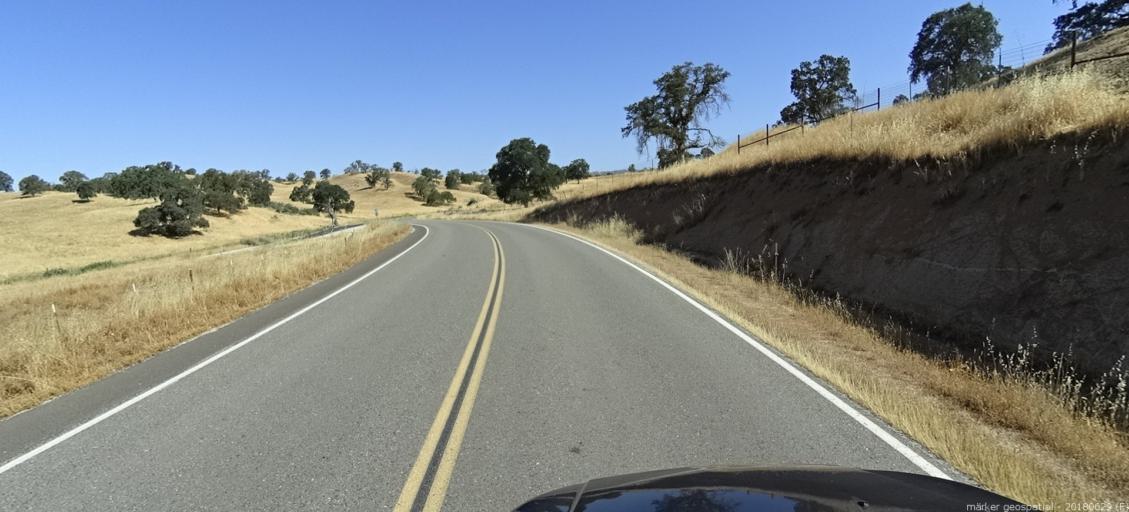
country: US
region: California
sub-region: Madera County
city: Bonadelle Ranchos-Madera Ranchos
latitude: 37.0610
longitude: -119.7899
